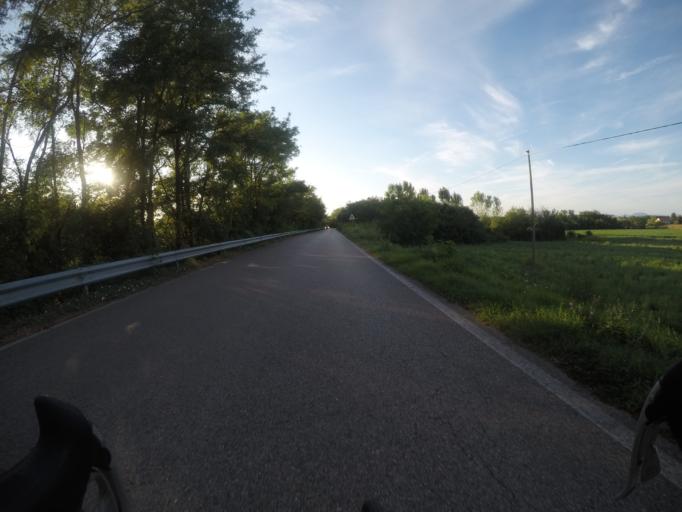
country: IT
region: Veneto
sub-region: Provincia di Rovigo
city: Castelguglielmo
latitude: 45.0173
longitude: 11.5643
